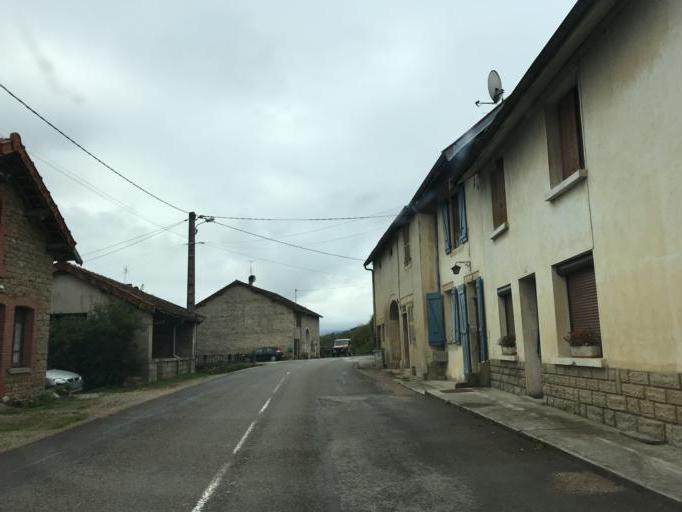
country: FR
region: Franche-Comte
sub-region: Departement du Jura
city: Arinthod
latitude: 46.4640
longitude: 5.5604
